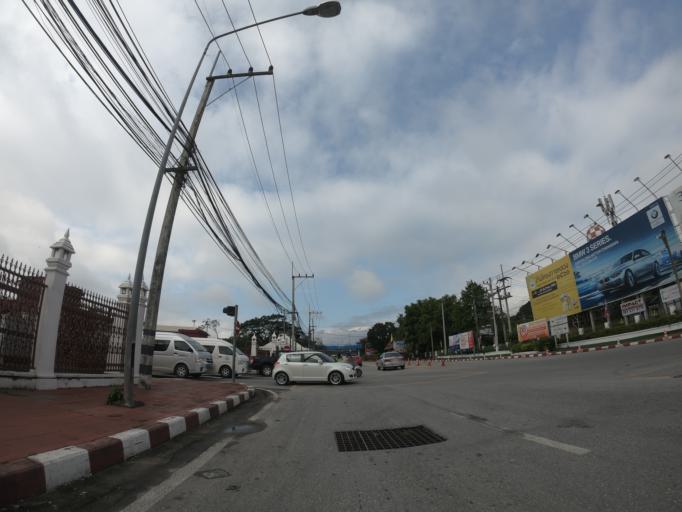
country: TH
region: Chiang Mai
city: Chiang Mai
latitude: 18.7722
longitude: 98.9684
